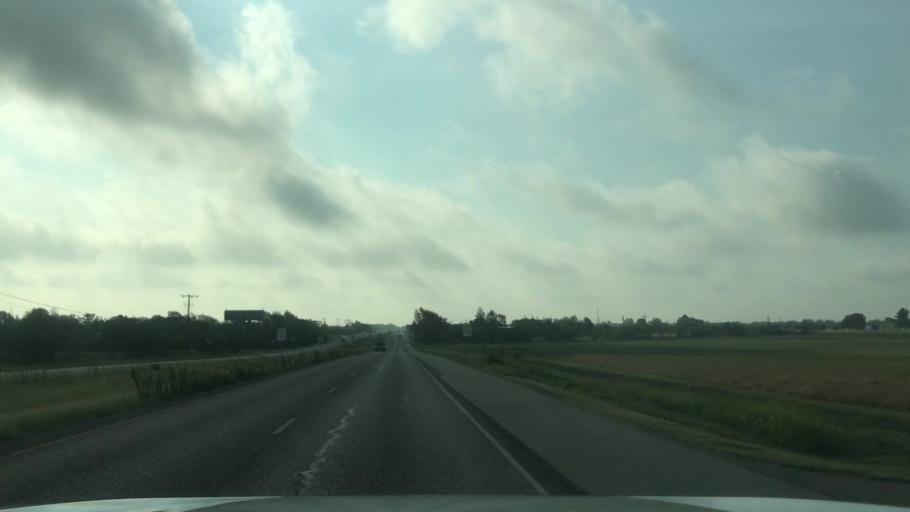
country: US
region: Texas
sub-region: Garza County
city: Post
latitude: 33.2064
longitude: -101.3983
